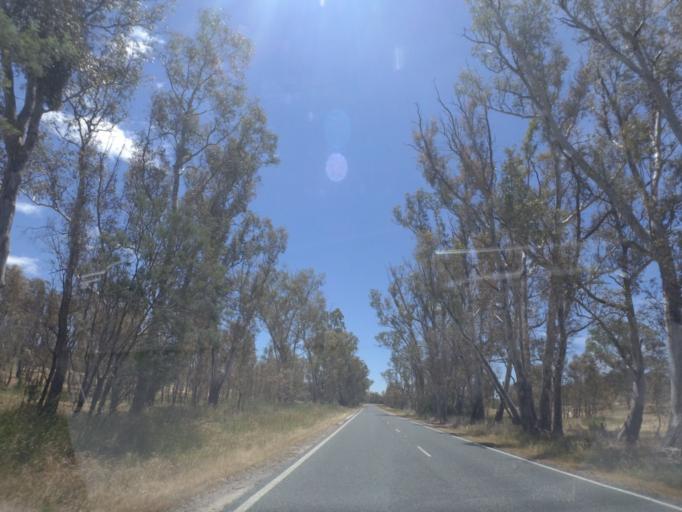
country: AU
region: Victoria
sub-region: Mount Alexander
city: Castlemaine
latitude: -37.1764
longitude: 144.1471
